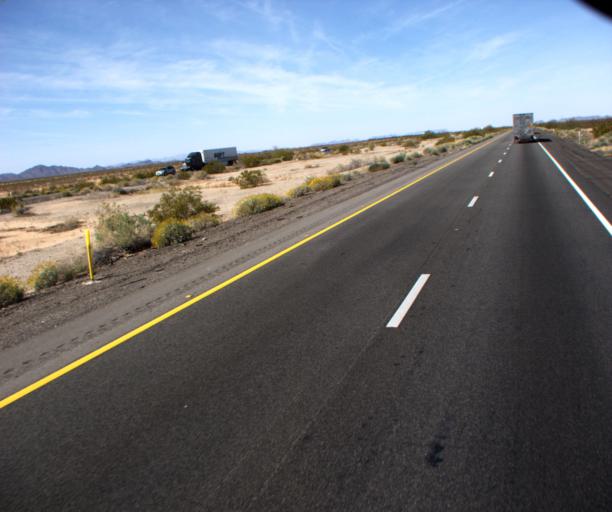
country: US
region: Arizona
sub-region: La Paz County
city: Salome
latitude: 33.5770
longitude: -113.4040
